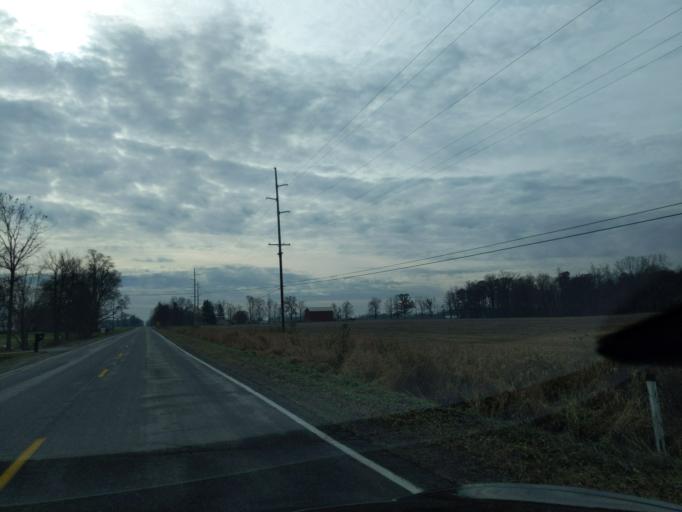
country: US
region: Michigan
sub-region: Ingham County
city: Holt
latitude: 42.6147
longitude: -84.5231
